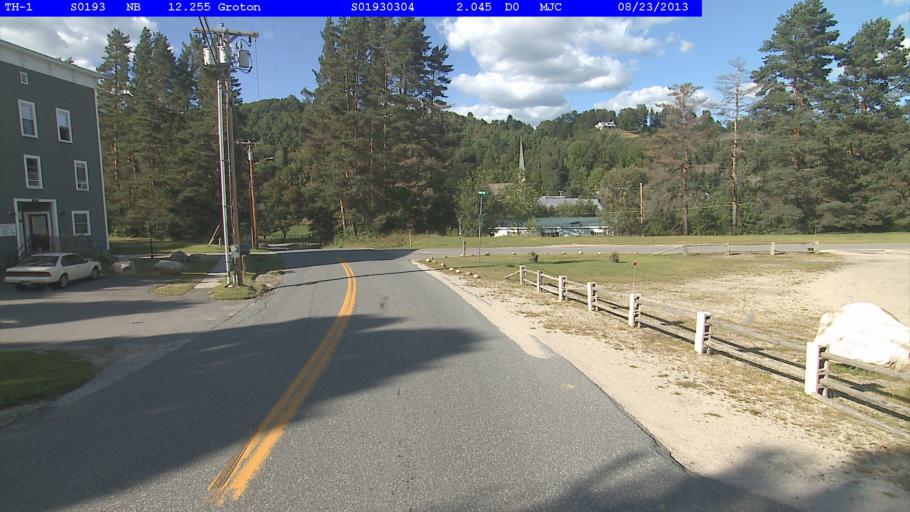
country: US
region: New Hampshire
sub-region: Grafton County
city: Woodsville
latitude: 44.2086
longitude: -72.1971
